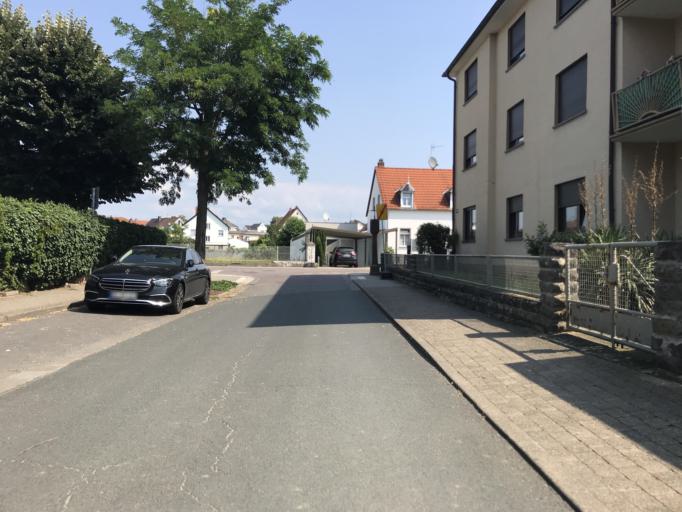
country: DE
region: Hesse
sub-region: Regierungsbezirk Darmstadt
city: Hochheim am Main
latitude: 50.0102
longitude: 8.3559
